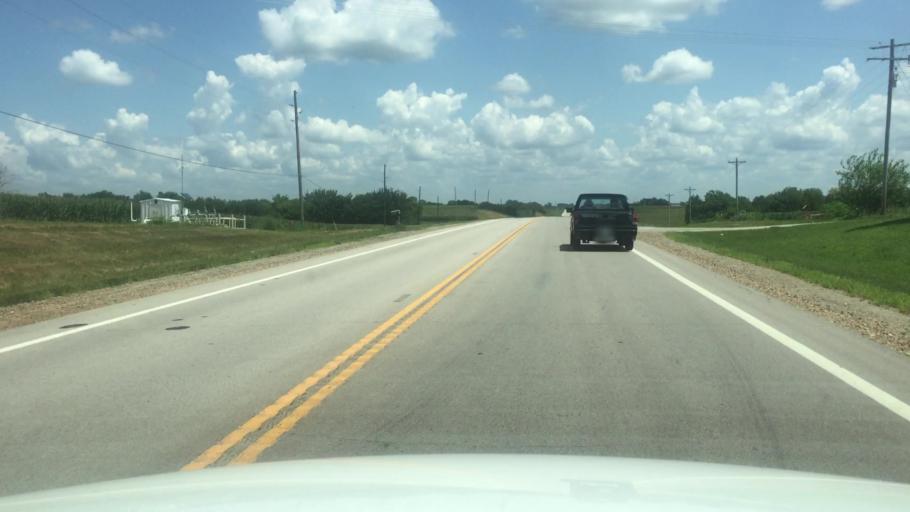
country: US
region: Kansas
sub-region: Brown County
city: Horton
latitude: 39.6674
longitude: -95.5081
